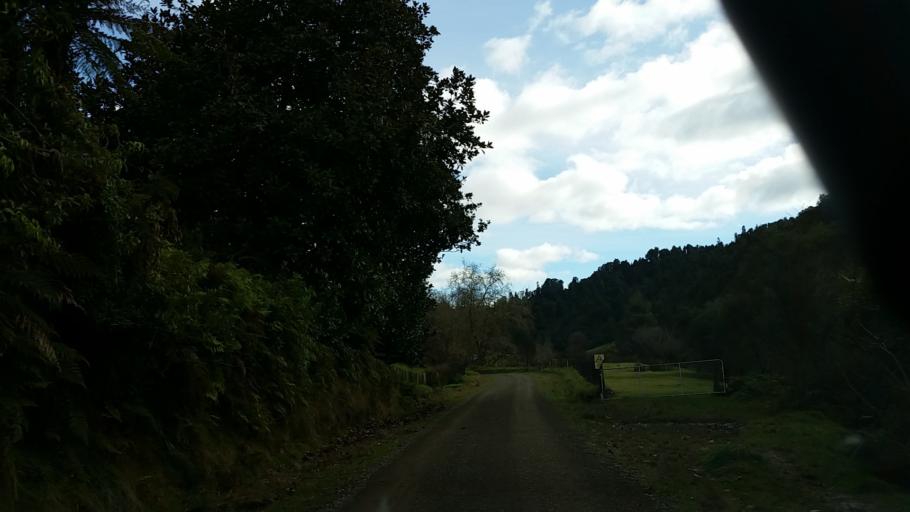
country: NZ
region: Taranaki
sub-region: New Plymouth District
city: Waitara
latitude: -39.0568
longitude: 174.5661
